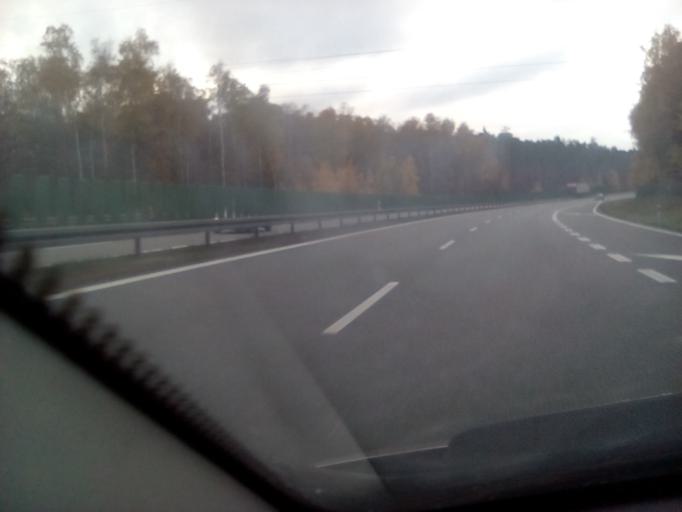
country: PL
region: Masovian Voivodeship
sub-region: Powiat bialobrzeski
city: Bialobrzegi
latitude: 51.6475
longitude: 20.9738
